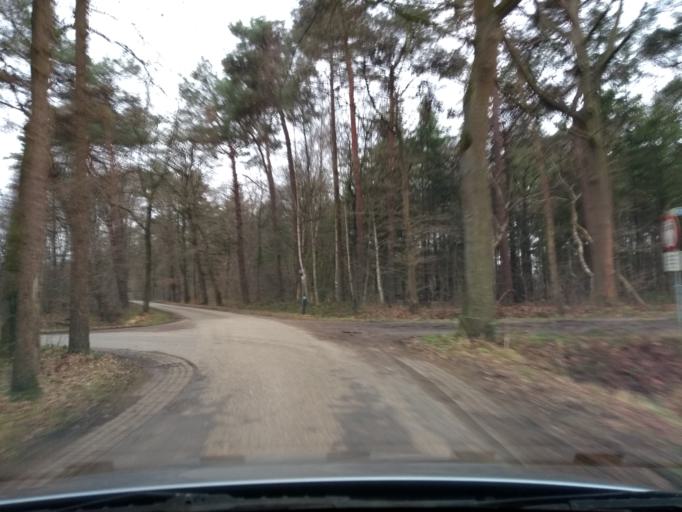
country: NL
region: Gelderland
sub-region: Gemeente Lochem
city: Barchem
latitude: 52.0689
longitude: 6.3931
